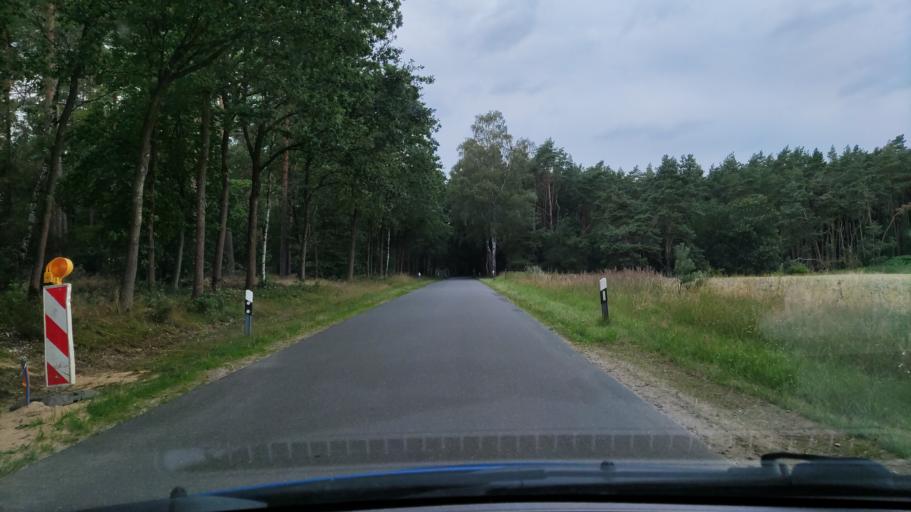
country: DE
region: Lower Saxony
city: Suhlendorf
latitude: 52.9682
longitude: 10.8232
